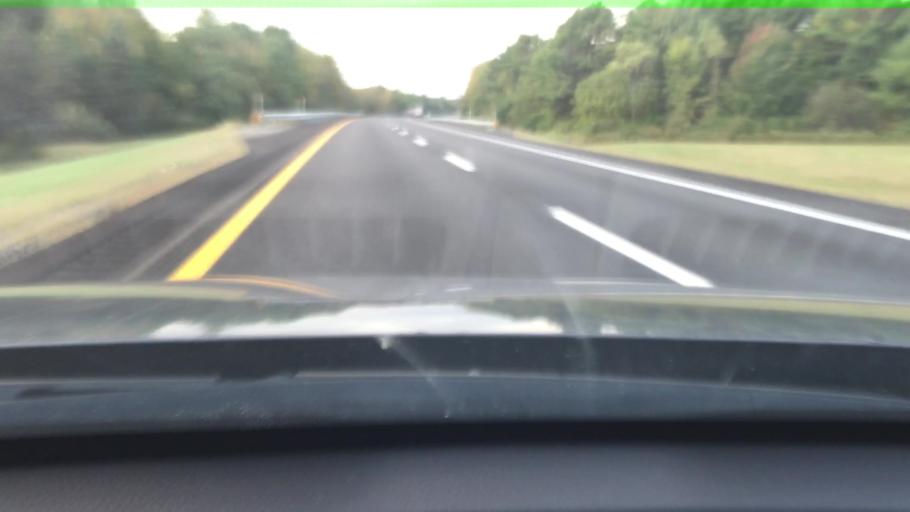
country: US
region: Maine
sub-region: Sagadahoc County
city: Richmond
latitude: 44.0655
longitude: -69.8831
